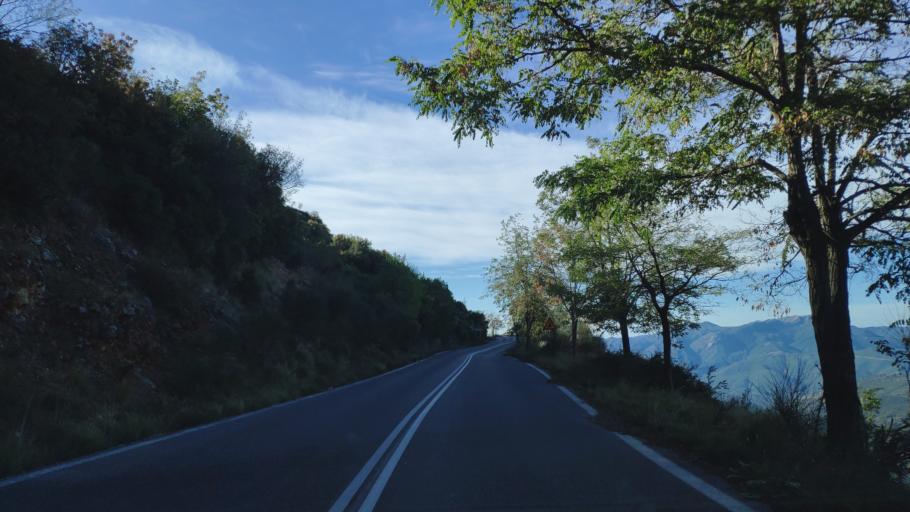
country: GR
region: Peloponnese
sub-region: Nomos Arkadias
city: Dimitsana
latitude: 37.5578
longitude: 22.0636
